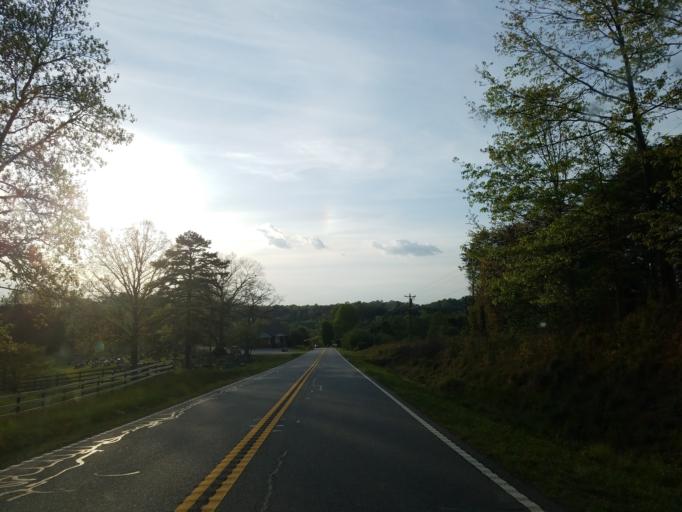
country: US
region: Georgia
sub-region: Fannin County
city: Blue Ridge
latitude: 34.8439
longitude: -84.2089
